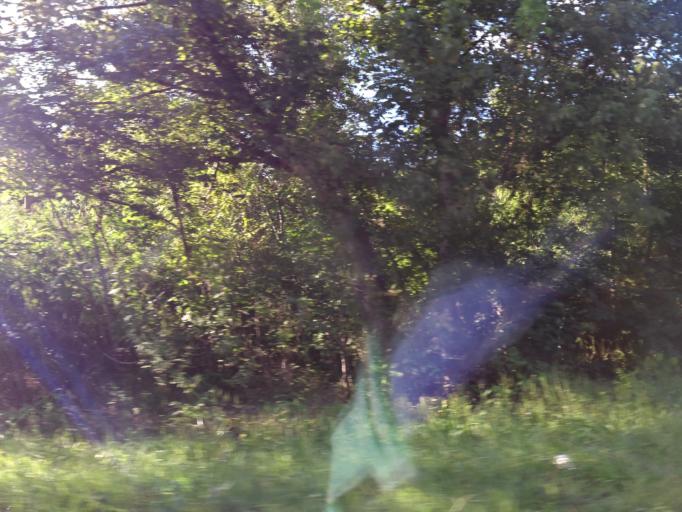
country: US
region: Tennessee
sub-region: Union County
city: Condon
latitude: 36.2013
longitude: -83.8016
